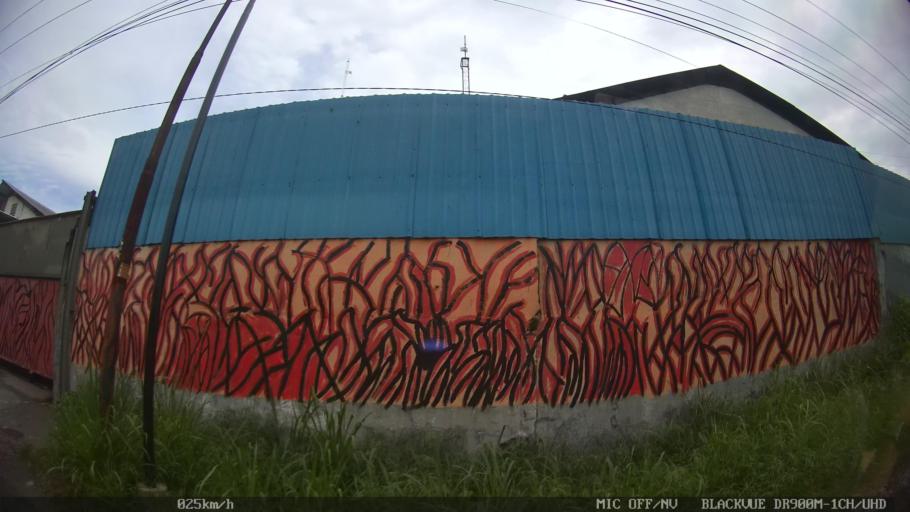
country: ID
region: North Sumatra
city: Sunggal
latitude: 3.6145
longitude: 98.5868
